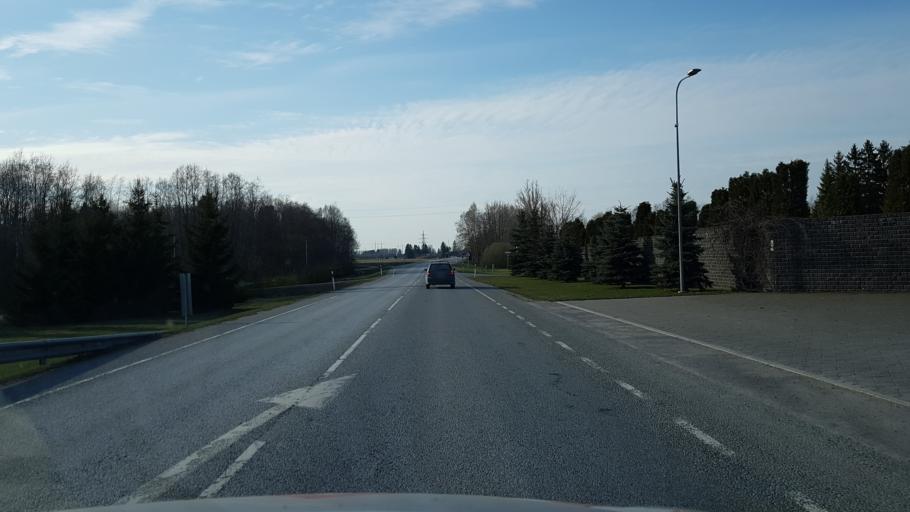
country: EE
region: Laeaene-Virumaa
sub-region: Rakvere linn
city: Rakvere
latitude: 59.3801
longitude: 26.3227
